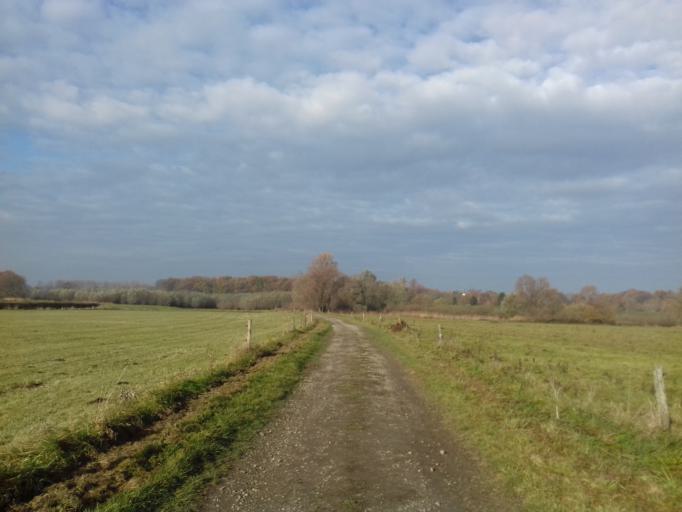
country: NL
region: Gelderland
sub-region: Gemeente Neerijnen
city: Neerijnen
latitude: 51.8259
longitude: 5.2829
